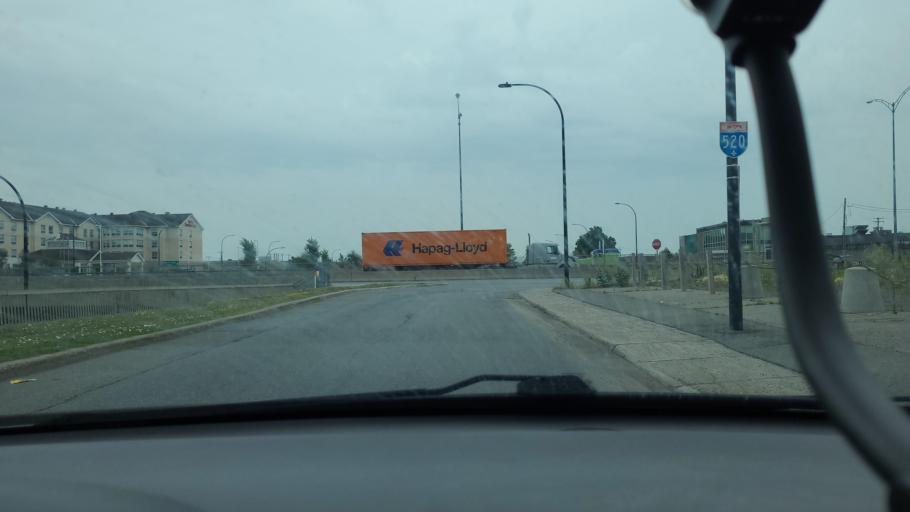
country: CA
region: Quebec
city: Cote-Saint-Luc
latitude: 45.4774
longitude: -73.7039
